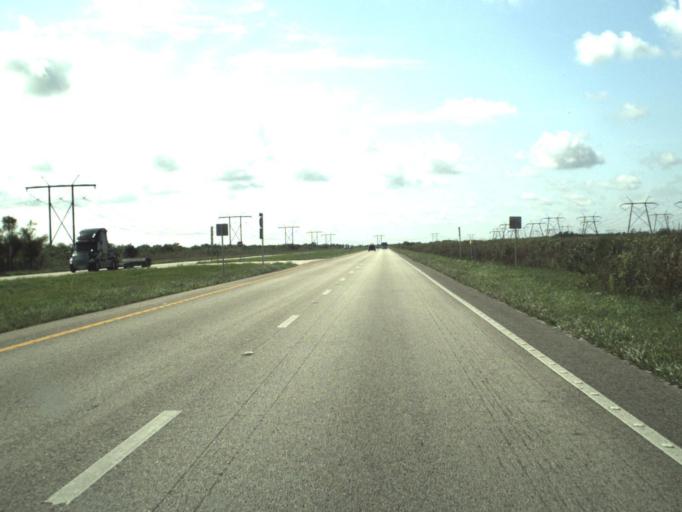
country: US
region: Florida
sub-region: Broward County
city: Weston
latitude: 26.2529
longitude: -80.4747
